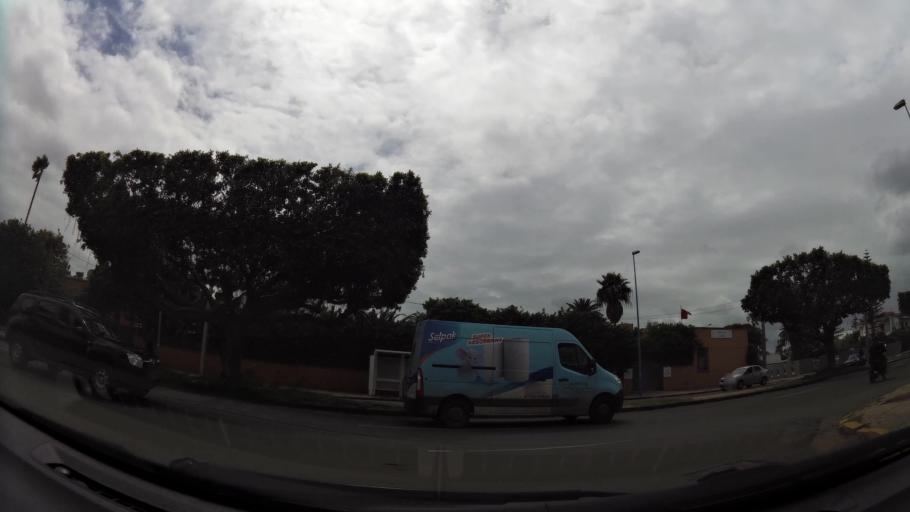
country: MA
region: Grand Casablanca
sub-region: Casablanca
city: Casablanca
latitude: 33.5605
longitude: -7.6397
